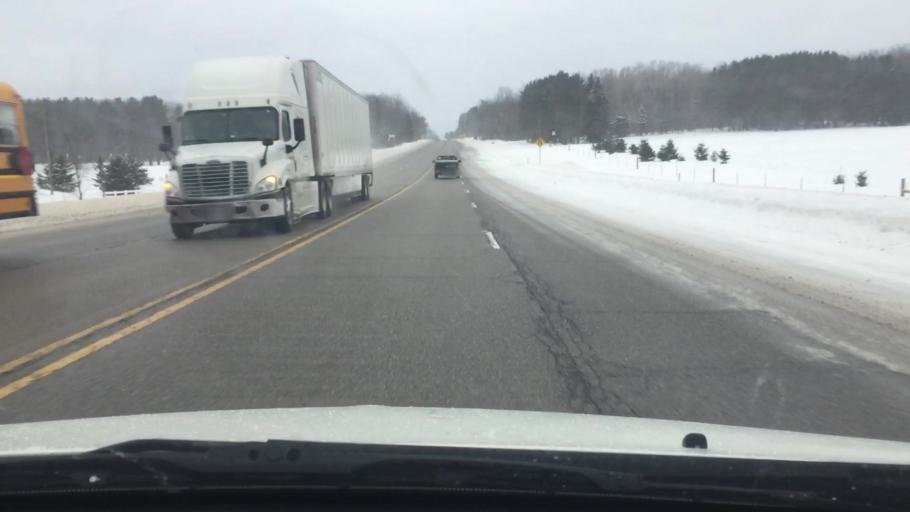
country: US
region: Michigan
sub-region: Otsego County
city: Gaylord
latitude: 45.0513
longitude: -84.7759
